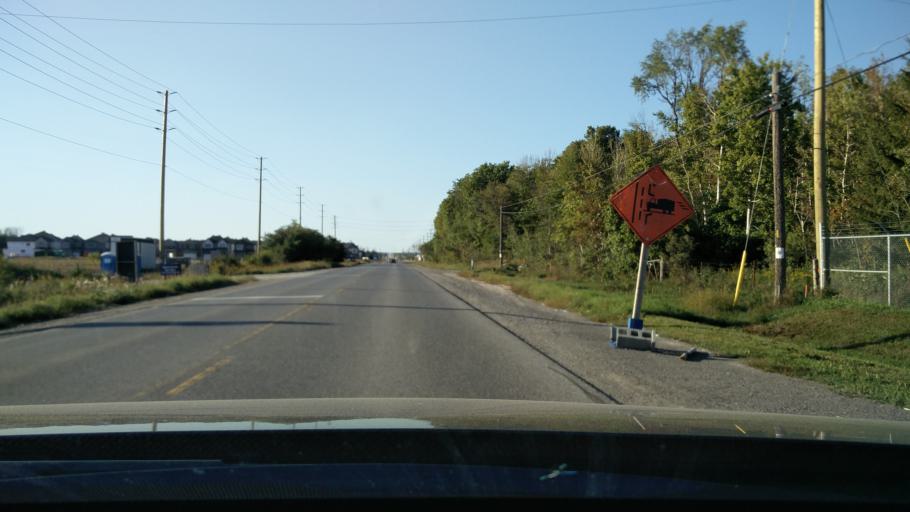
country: CA
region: Ontario
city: Bells Corners
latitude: 45.2369
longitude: -75.7264
